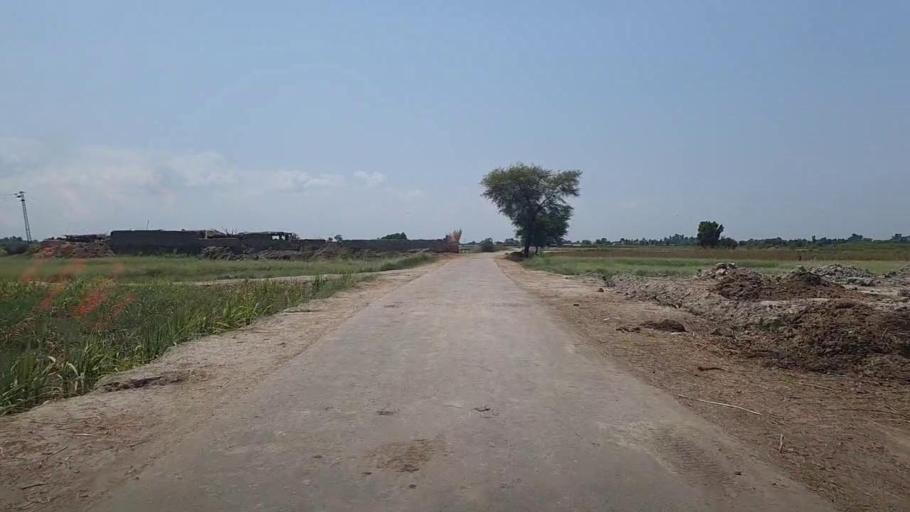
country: PK
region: Sindh
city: Ubauro
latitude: 28.1916
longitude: 69.7999
